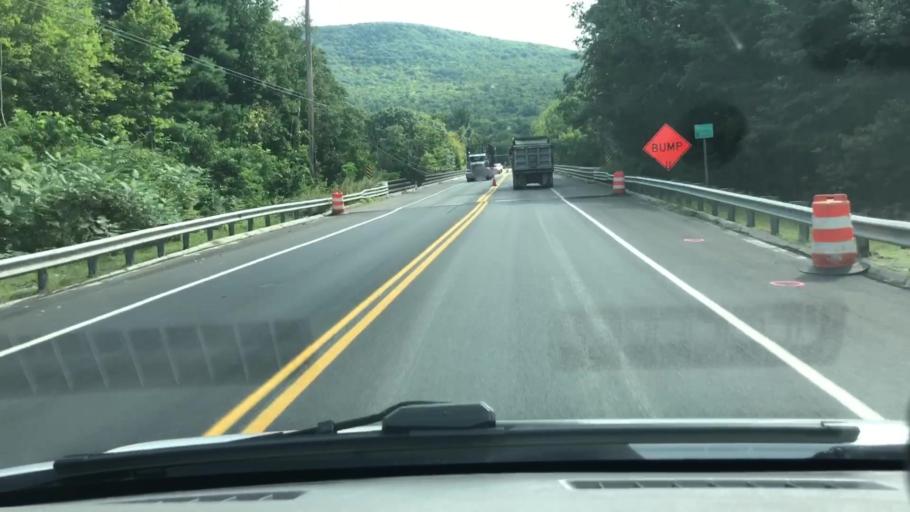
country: US
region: Massachusetts
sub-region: Franklin County
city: Shelburne Falls
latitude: 42.6140
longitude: -72.7383
